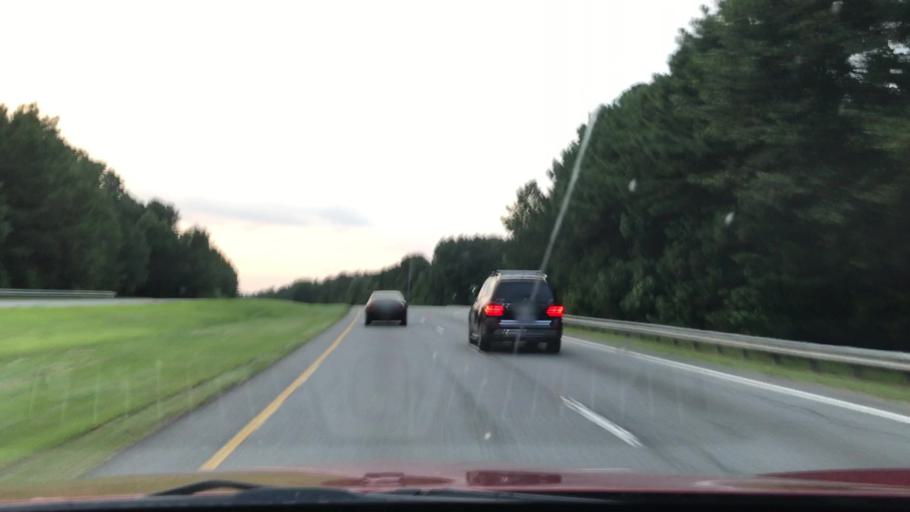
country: US
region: Georgia
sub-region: Gwinnett County
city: Lawrenceville
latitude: 34.0293
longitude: -83.9863
